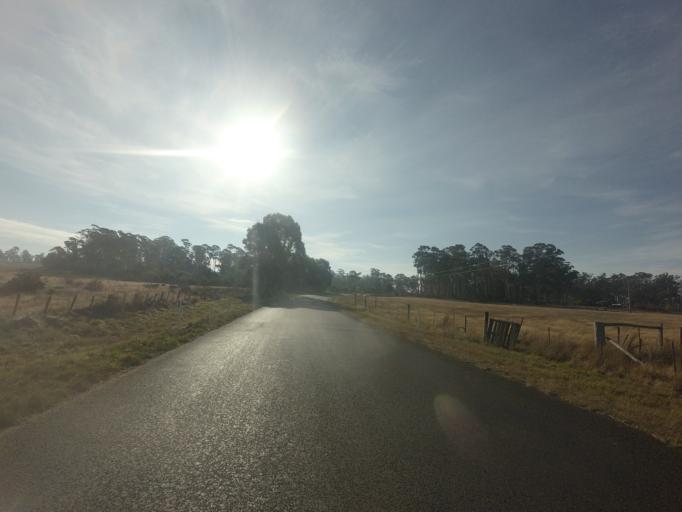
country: AU
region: Tasmania
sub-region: Sorell
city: Sorell
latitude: -42.4700
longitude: 147.4616
